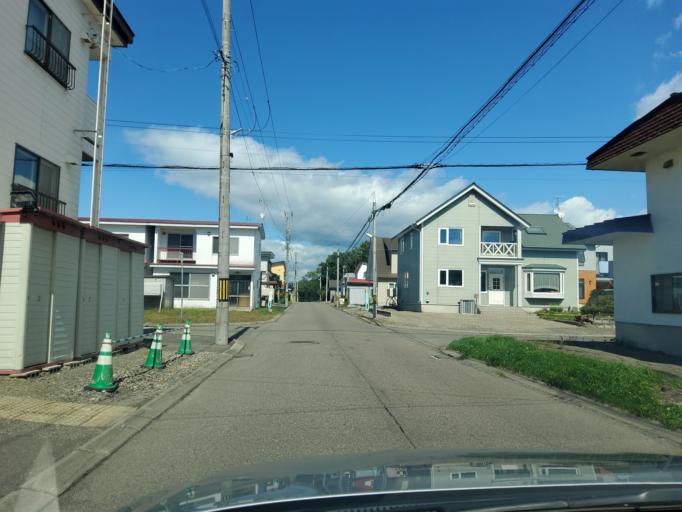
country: JP
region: Hokkaido
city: Obihiro
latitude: 42.9502
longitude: 143.1981
